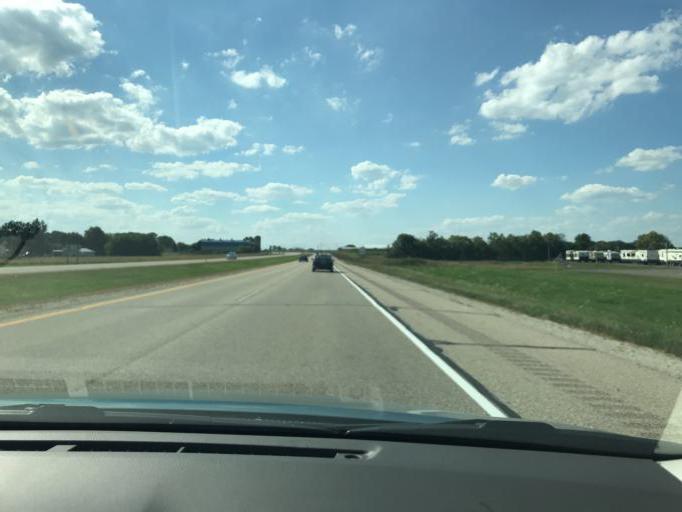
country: US
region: Wisconsin
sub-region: Kenosha County
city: Powers Lake
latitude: 42.5837
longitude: -88.2873
